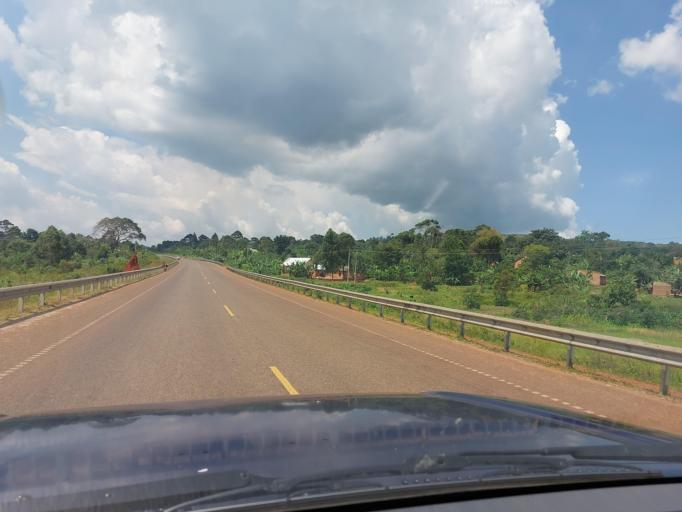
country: UG
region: Central Region
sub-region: Buikwe District
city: Buikwe
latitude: 0.3210
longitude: 33.1128
